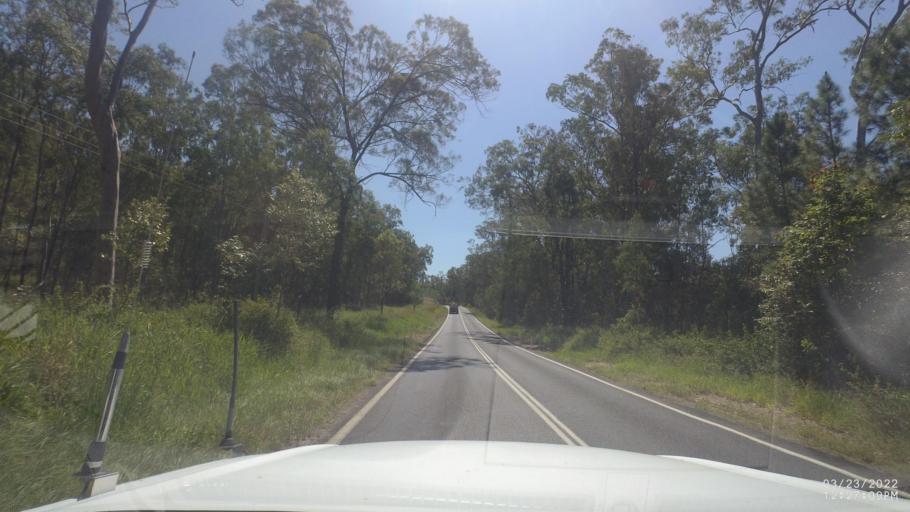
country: AU
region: Queensland
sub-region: Logan
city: Chambers Flat
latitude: -27.8274
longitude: 153.1047
